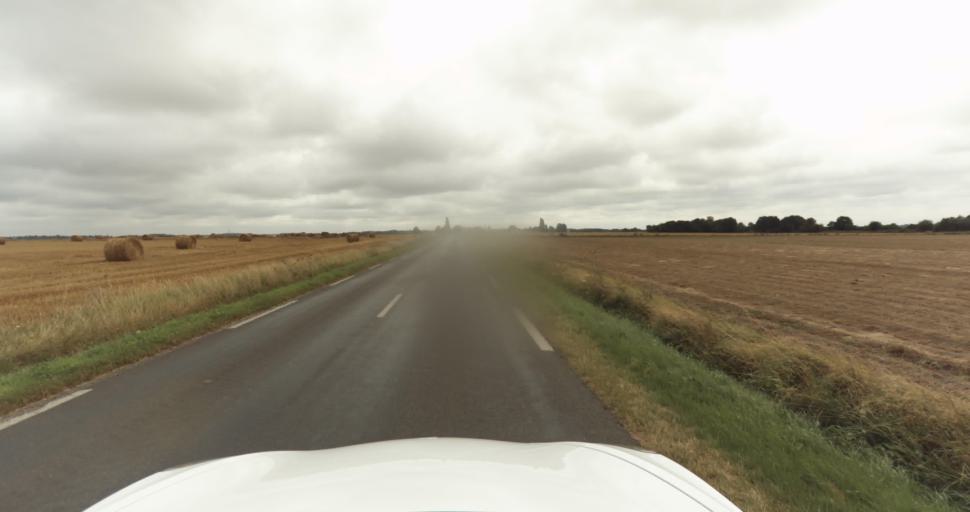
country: FR
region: Haute-Normandie
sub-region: Departement de l'Eure
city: Claville
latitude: 49.0753
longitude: 1.0632
